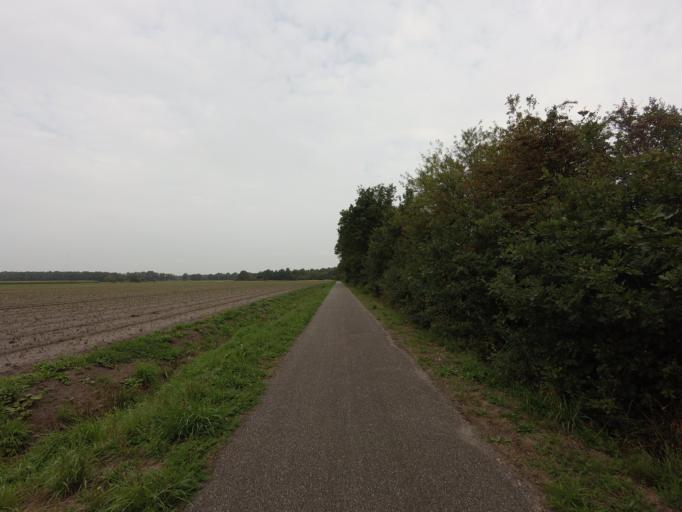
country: NL
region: Drenthe
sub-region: Gemeente Westerveld
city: Dwingeloo
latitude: 52.8924
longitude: 6.4623
